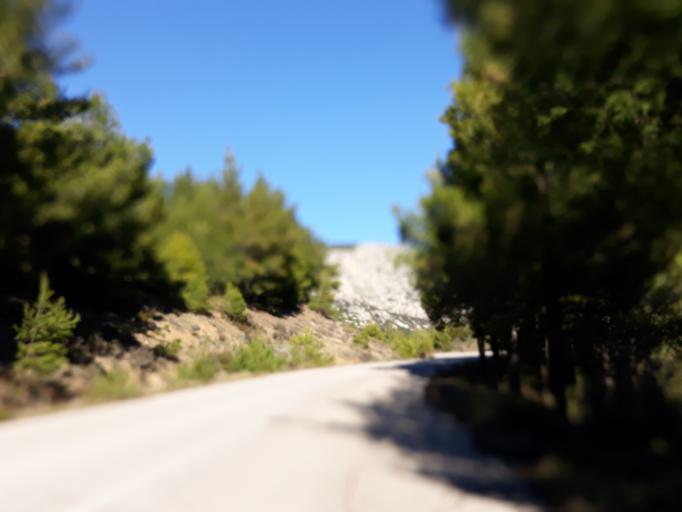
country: GR
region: Attica
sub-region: Nomarchia Dytikis Attikis
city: Fyli
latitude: 38.1248
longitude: 23.6483
